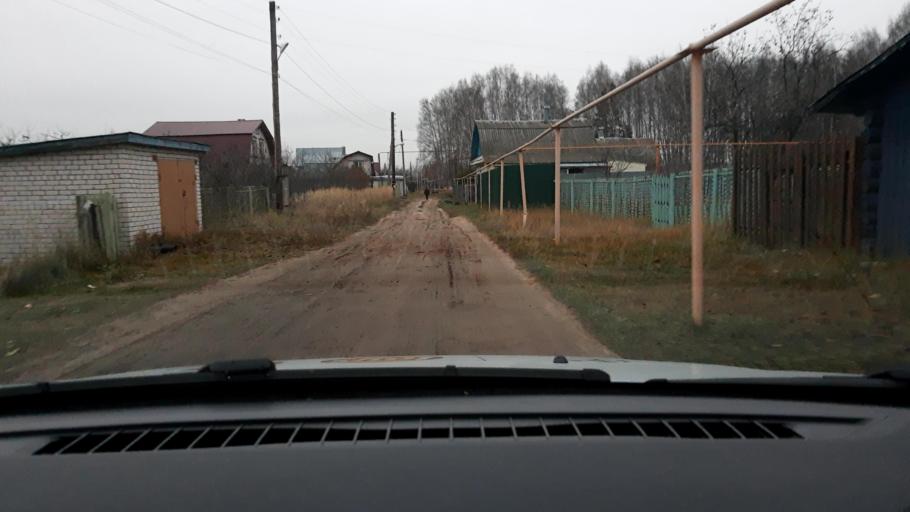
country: RU
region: Nizjnij Novgorod
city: Neklyudovo
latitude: 56.4243
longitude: 44.0119
